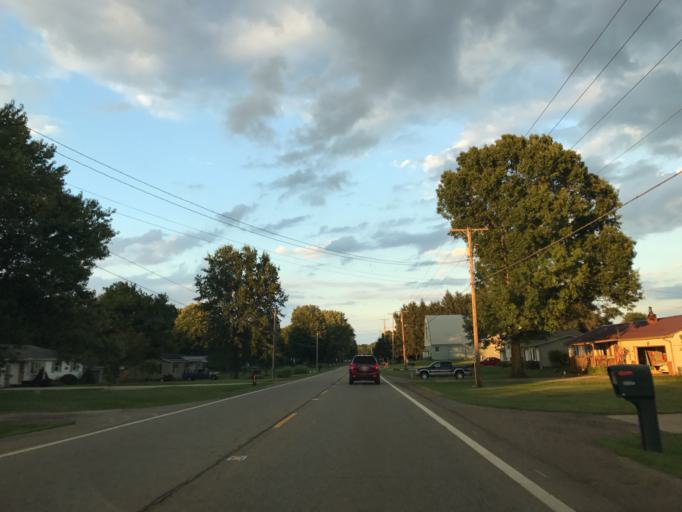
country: US
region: Ohio
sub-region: Stark County
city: Minerva
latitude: 40.7446
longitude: -81.0761
